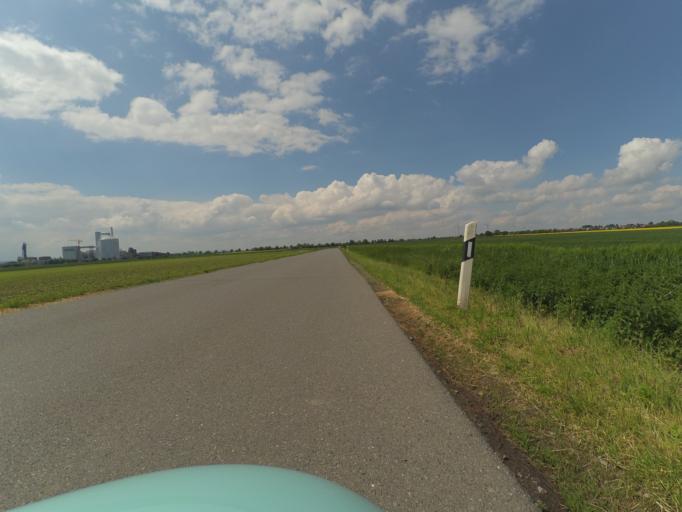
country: DE
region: Lower Saxony
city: Hohenhameln
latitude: 52.2393
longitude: 10.0458
